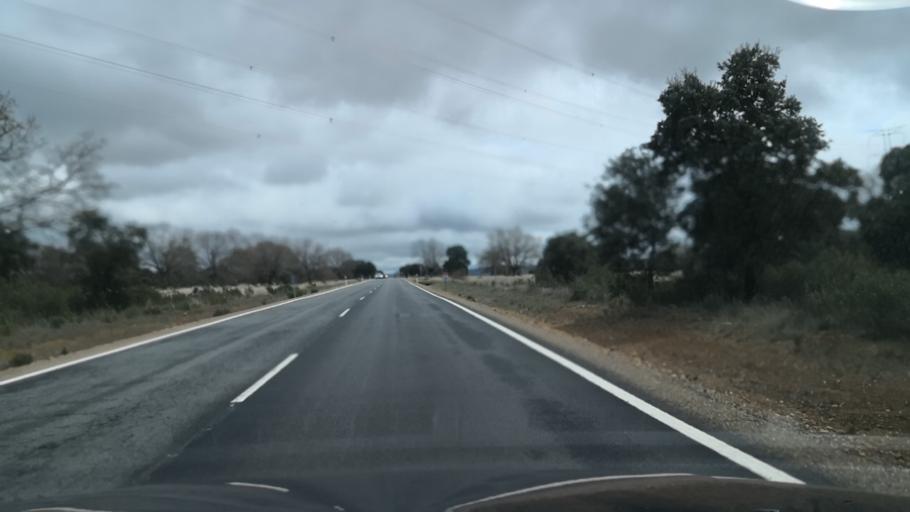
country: ES
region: Castille and Leon
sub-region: Provincia de Zamora
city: Tabara
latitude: 41.8085
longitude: -5.9309
